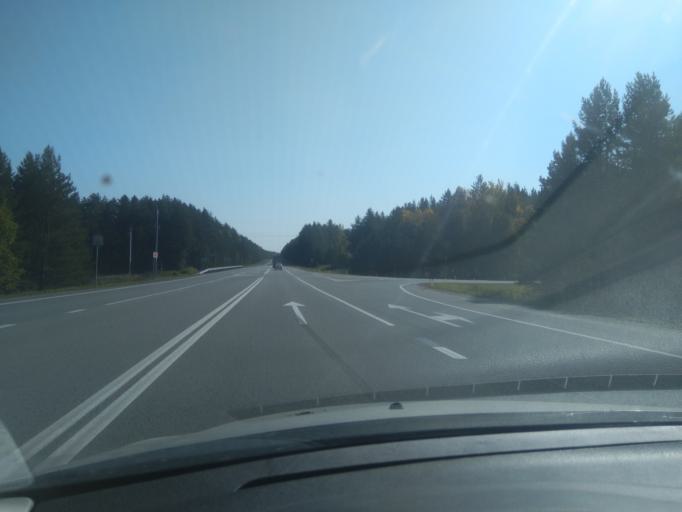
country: RU
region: Sverdlovsk
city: Verkhneye Dubrovo
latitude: 56.6985
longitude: 61.0888
